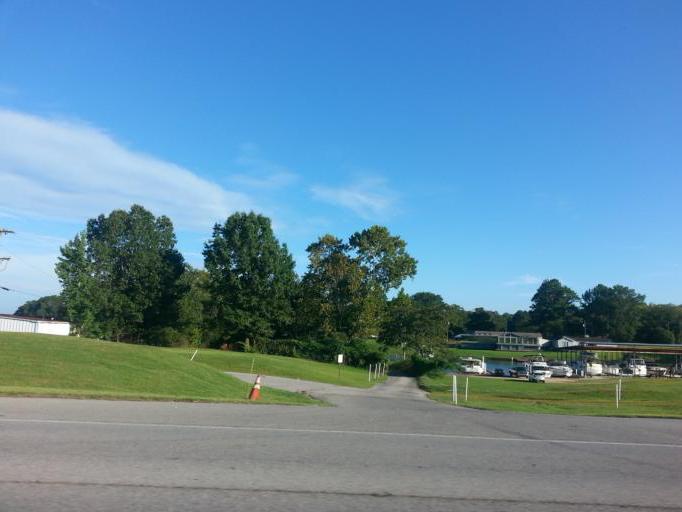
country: US
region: Alabama
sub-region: Lauderdale County
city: Killen
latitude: 34.8502
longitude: -87.5714
